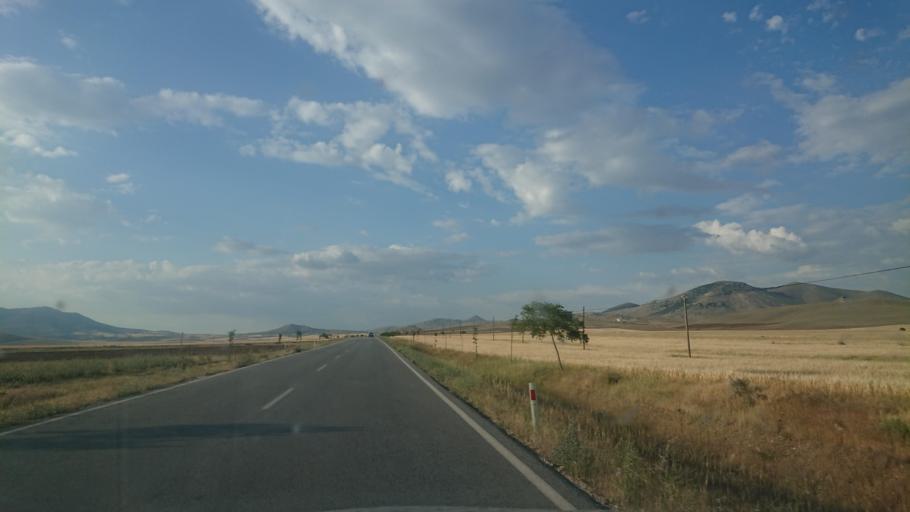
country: TR
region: Aksaray
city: Aksaray
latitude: 38.5168
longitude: 34.0914
